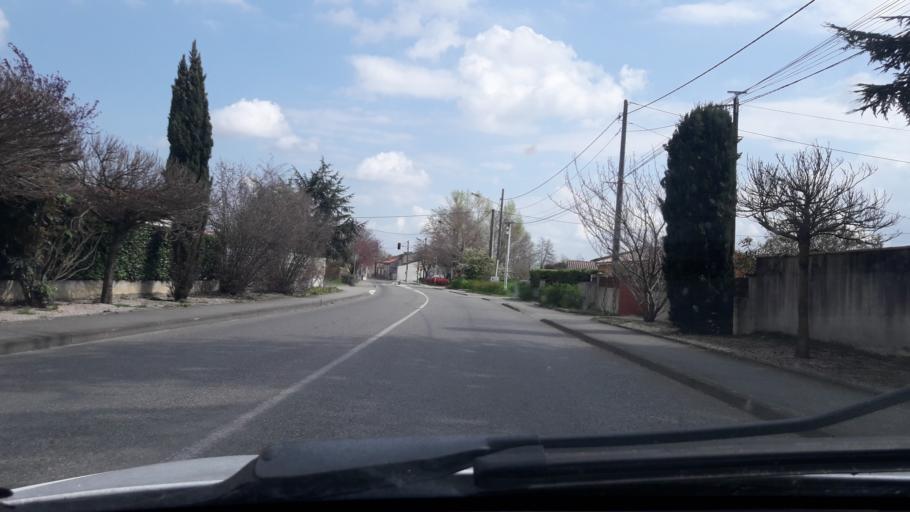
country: FR
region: Midi-Pyrenees
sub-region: Departement de la Haute-Garonne
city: Seysses
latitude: 43.4955
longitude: 1.3047
